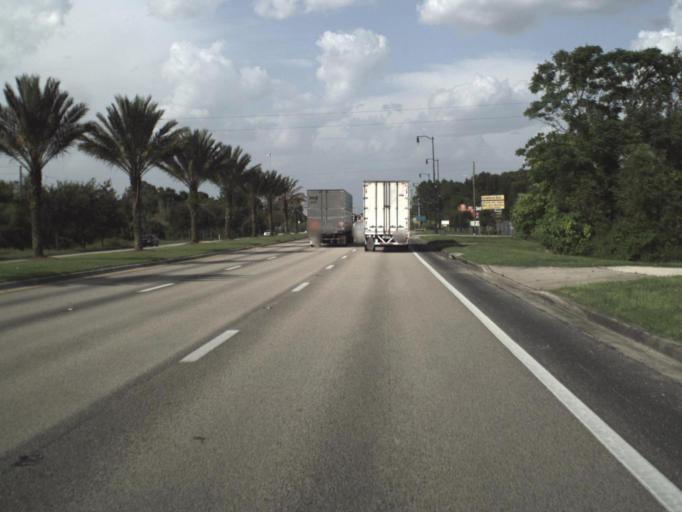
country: US
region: Florida
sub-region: Polk County
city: Haines City
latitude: 28.1012
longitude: -81.6453
